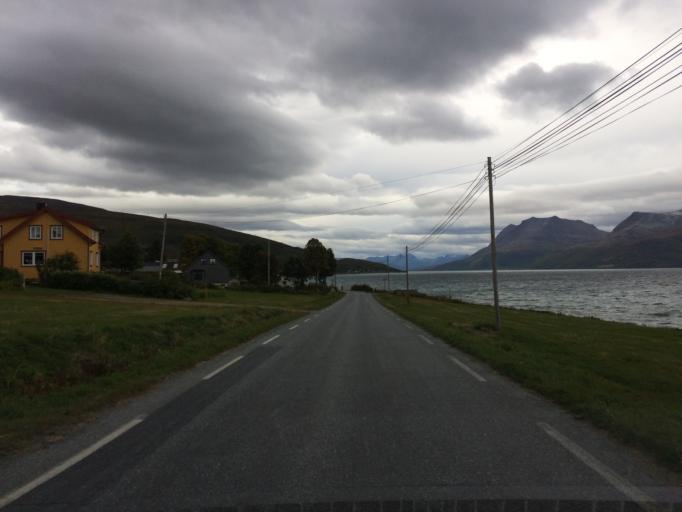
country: NO
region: Troms
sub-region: Sorreisa
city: Sorreisa
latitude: 69.5260
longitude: 18.2688
